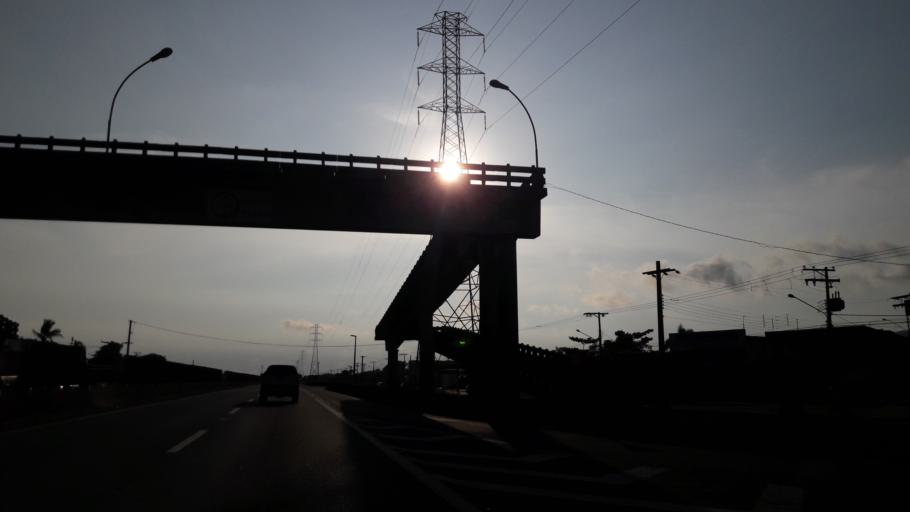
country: BR
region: Sao Paulo
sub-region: Itanhaem
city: Itanhaem
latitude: -24.1480
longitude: -46.7267
